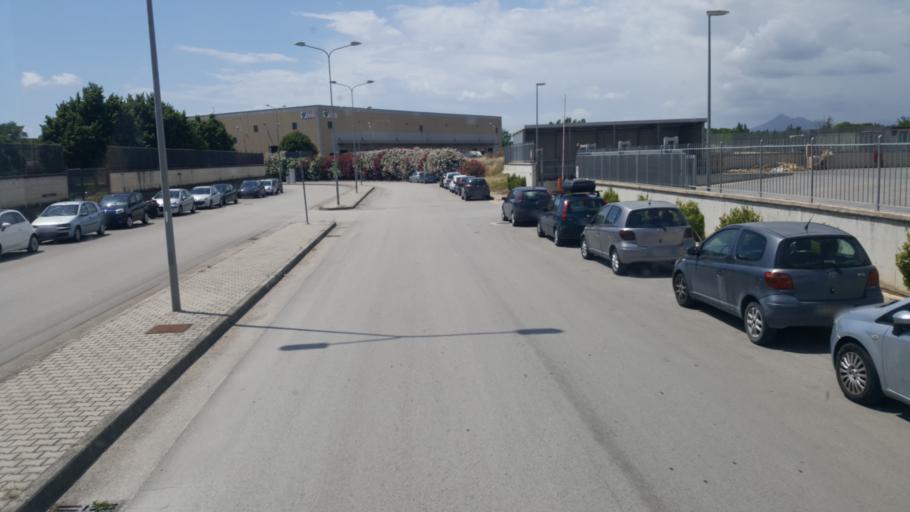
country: IT
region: Campania
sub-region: Provincia di Caserta
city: Maddaloni
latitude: 41.0096
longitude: 14.3669
